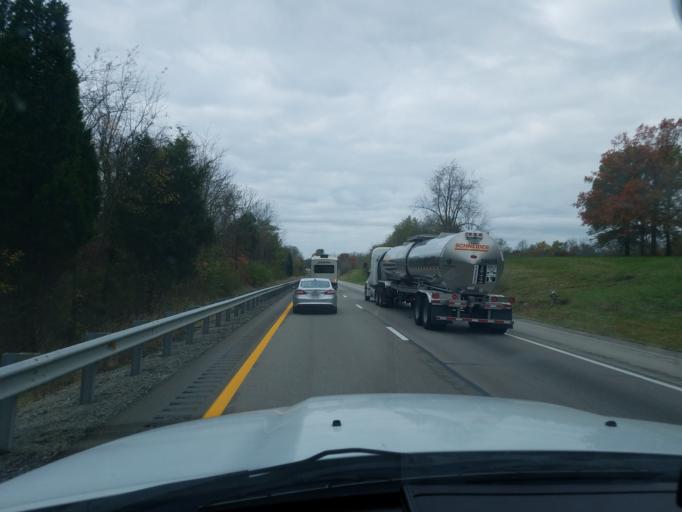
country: US
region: Indiana
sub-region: Switzerland County
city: Vevay
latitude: 38.6760
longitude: -85.0016
